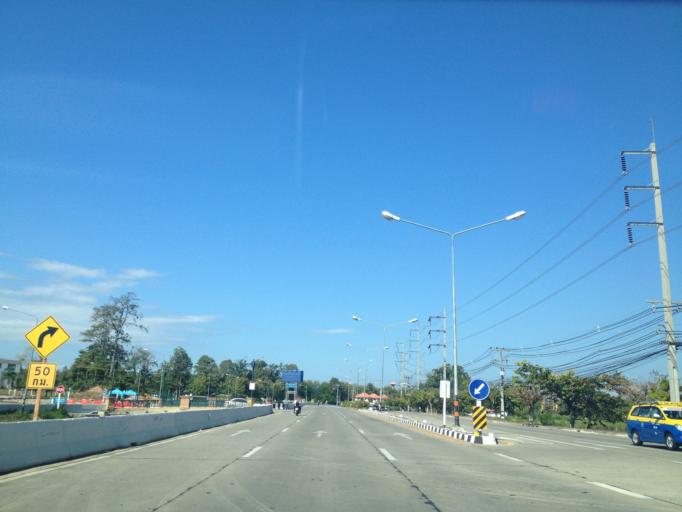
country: TH
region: Chiang Mai
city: Chiang Mai
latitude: 18.8301
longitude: 98.9637
